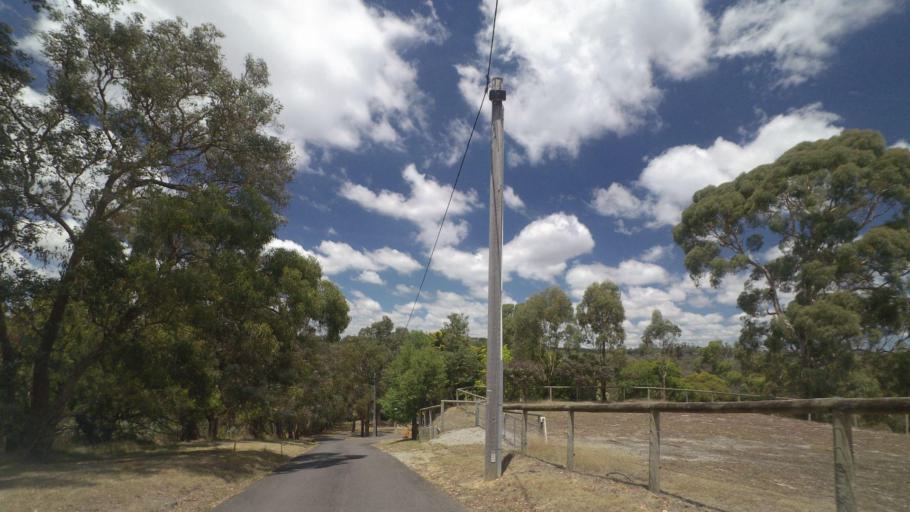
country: AU
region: Victoria
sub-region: Manningham
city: Warrandyte
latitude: -37.7444
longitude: 145.2497
